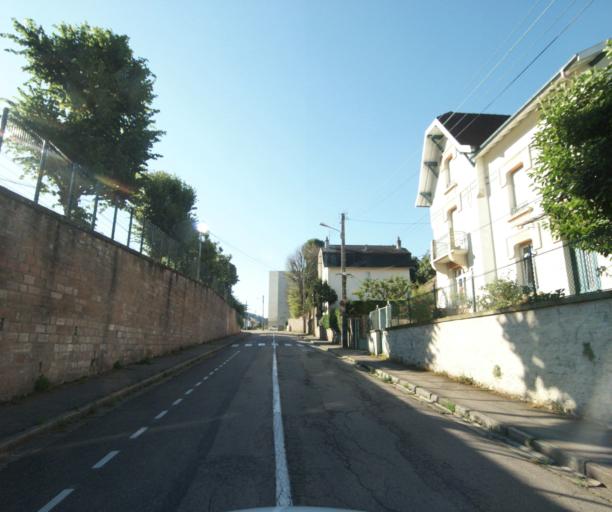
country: FR
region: Lorraine
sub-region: Departement des Vosges
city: Epinal
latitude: 48.1672
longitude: 6.4542
